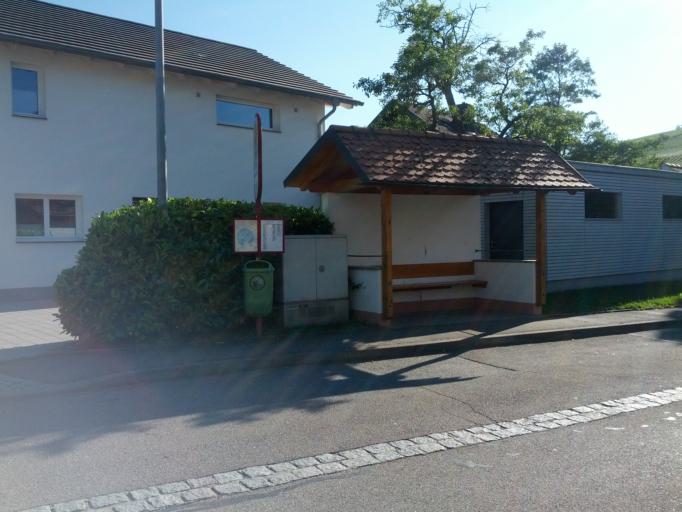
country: DE
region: Baden-Wuerttemberg
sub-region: Freiburg Region
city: Pfaffenweiler
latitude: 47.9413
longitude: 7.7546
